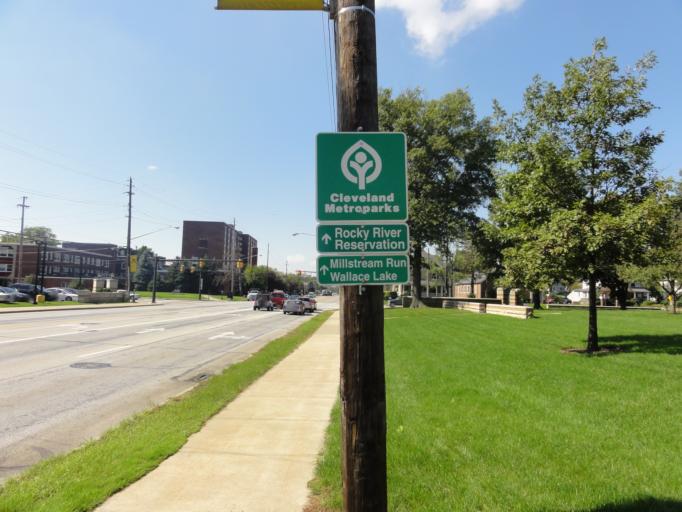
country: US
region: Ohio
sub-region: Cuyahoga County
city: Berea
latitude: 41.3728
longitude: -81.8512
